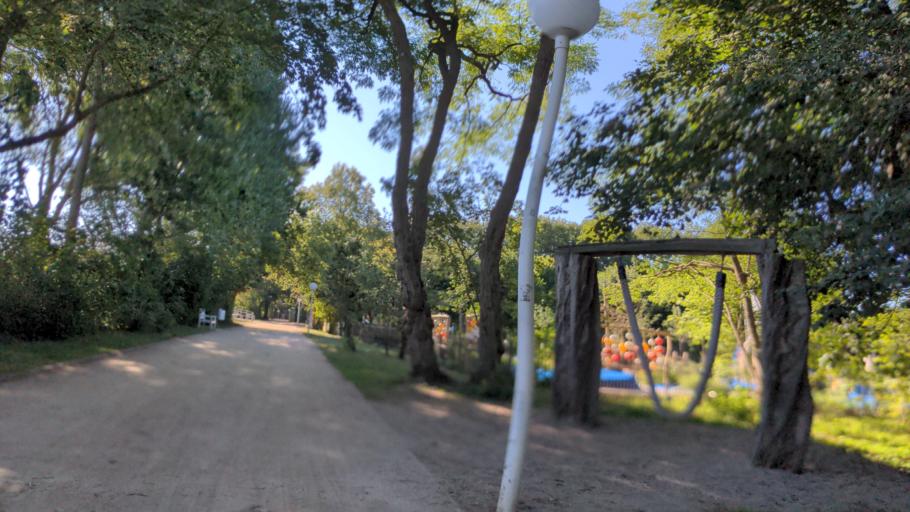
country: DE
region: Mecklenburg-Vorpommern
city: Ostseebad Boltenhagen
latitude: 53.9865
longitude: 11.2094
